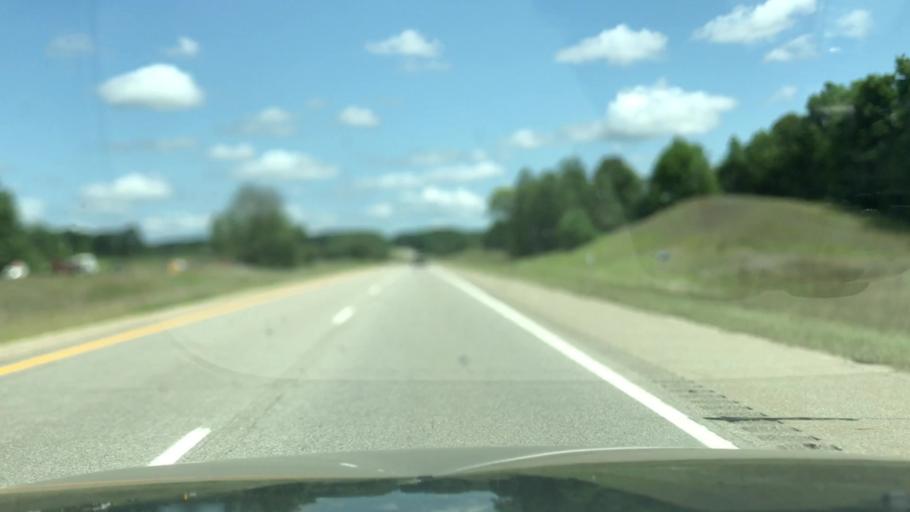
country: US
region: Michigan
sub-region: Osceola County
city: Reed City
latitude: 43.7961
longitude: -85.5337
